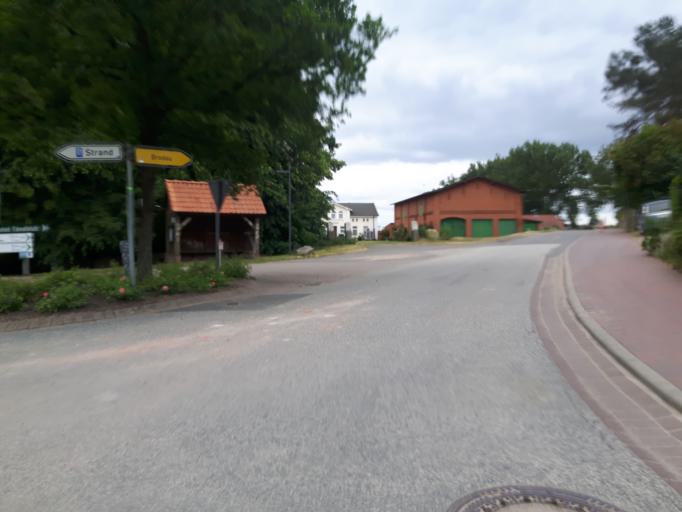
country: DE
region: Schleswig-Holstein
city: Schashagen
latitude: 54.1306
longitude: 10.9103
